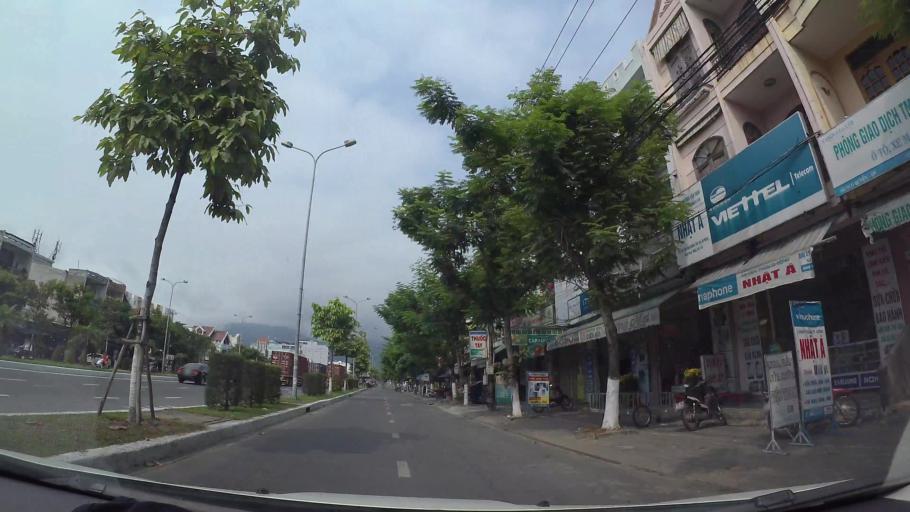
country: VN
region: Da Nang
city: Son Tra
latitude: 16.0876
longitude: 108.2416
